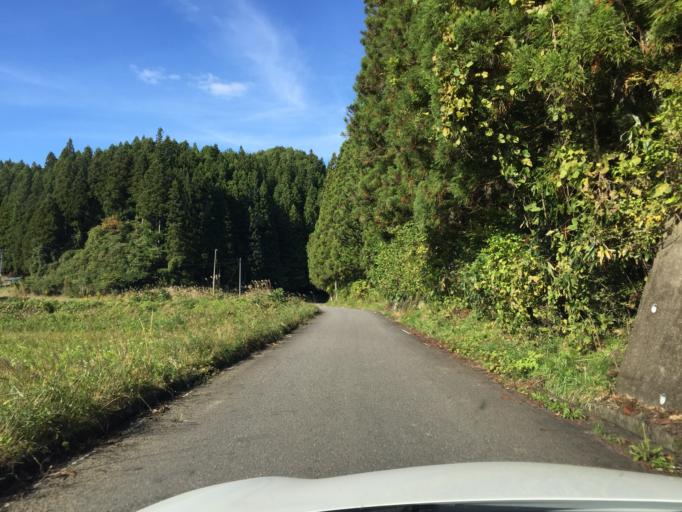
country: JP
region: Fukushima
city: Ishikawa
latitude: 37.1304
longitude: 140.5519
